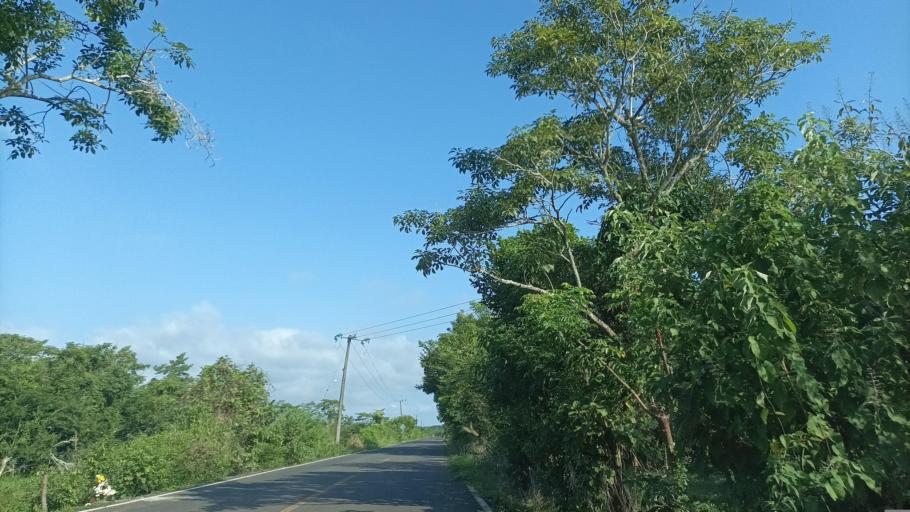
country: MX
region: Veracruz
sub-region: Chinameca
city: Chacalapa
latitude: 18.1407
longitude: -94.6529
